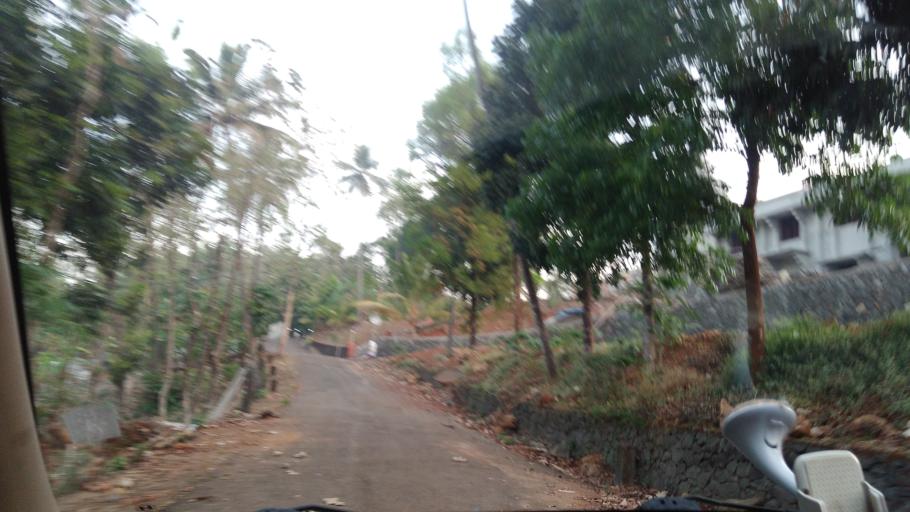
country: IN
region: Kerala
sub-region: Kottayam
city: Palackattumala
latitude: 9.8470
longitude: 76.6494
